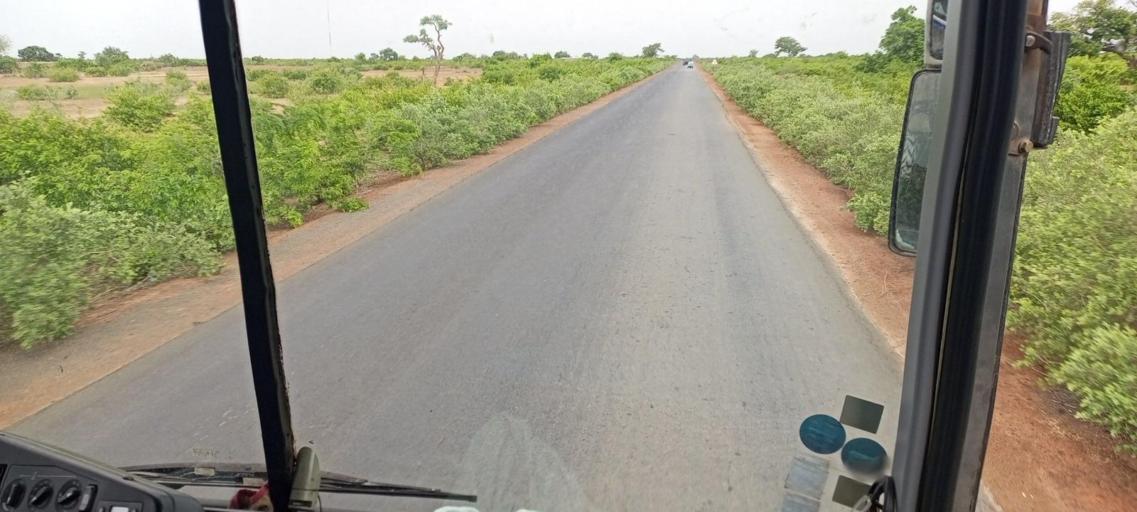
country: ML
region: Segou
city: Bla
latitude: 12.7598
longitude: -5.7376
